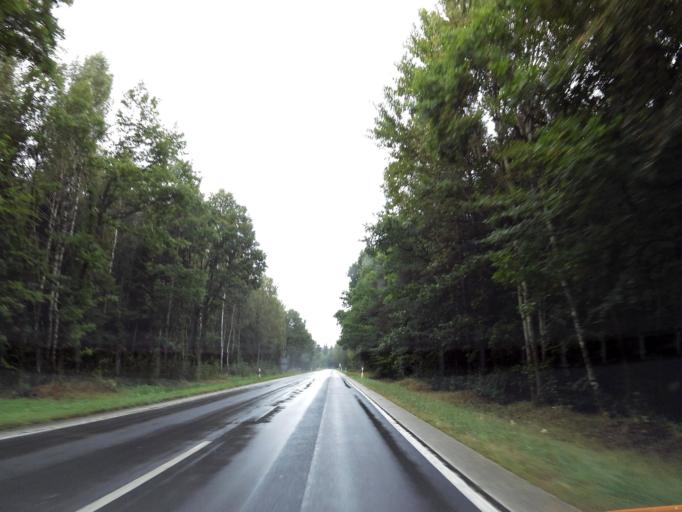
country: DE
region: Rheinland-Pfalz
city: Niederkumbd
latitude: 50.0234
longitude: 7.5480
